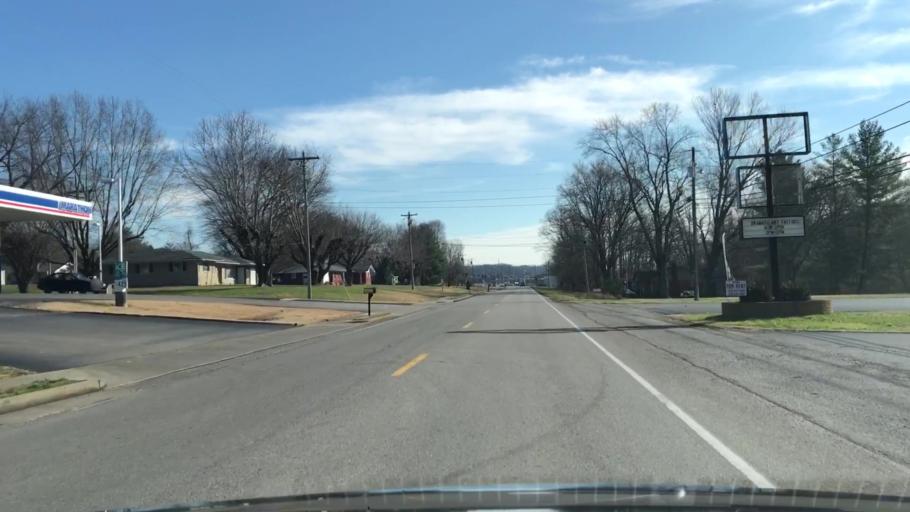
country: US
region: Kentucky
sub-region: Metcalfe County
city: Edmonton
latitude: 36.9856
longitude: -85.6314
